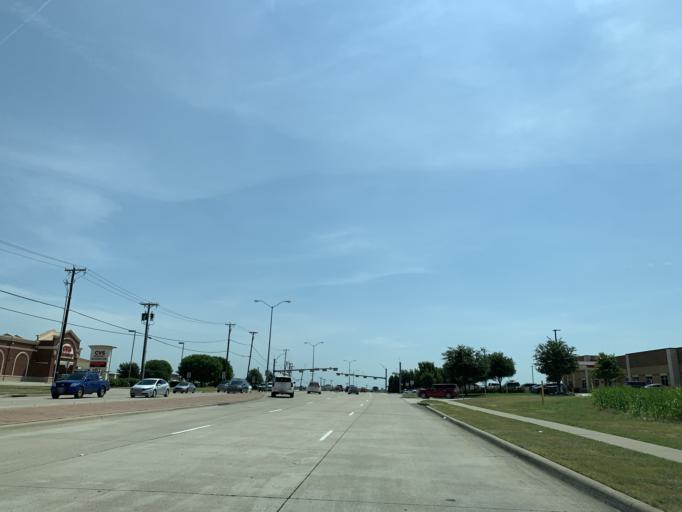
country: US
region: Texas
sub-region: Dallas County
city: Cedar Hill
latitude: 32.6478
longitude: -97.0458
